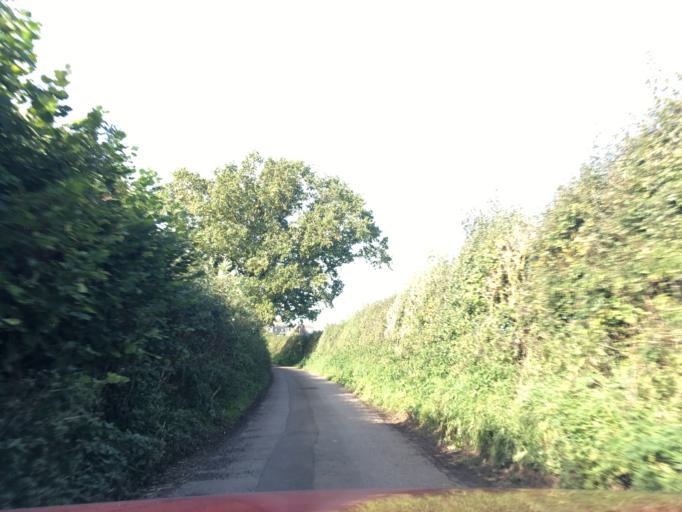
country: GB
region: England
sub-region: South Gloucestershire
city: Charfield
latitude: 51.6144
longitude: -2.4336
